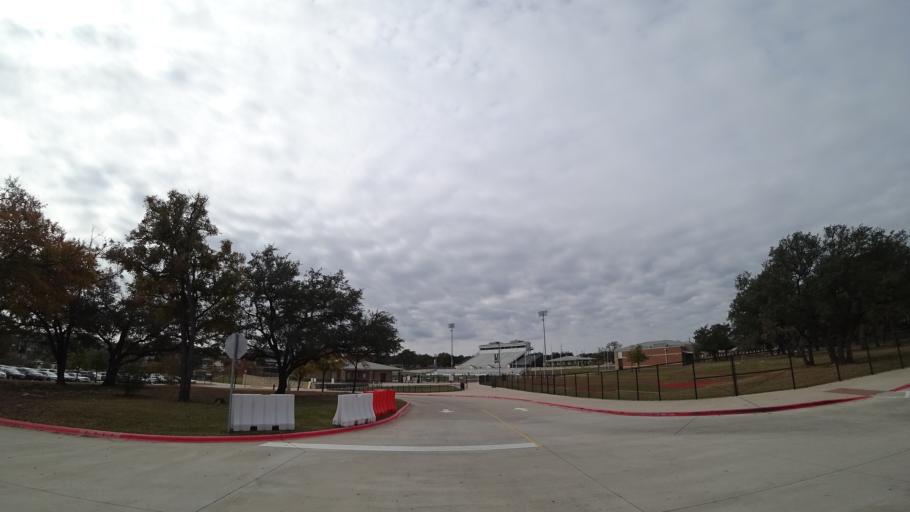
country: US
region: Texas
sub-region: Williamson County
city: Anderson Mill
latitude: 30.3976
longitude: -97.8264
